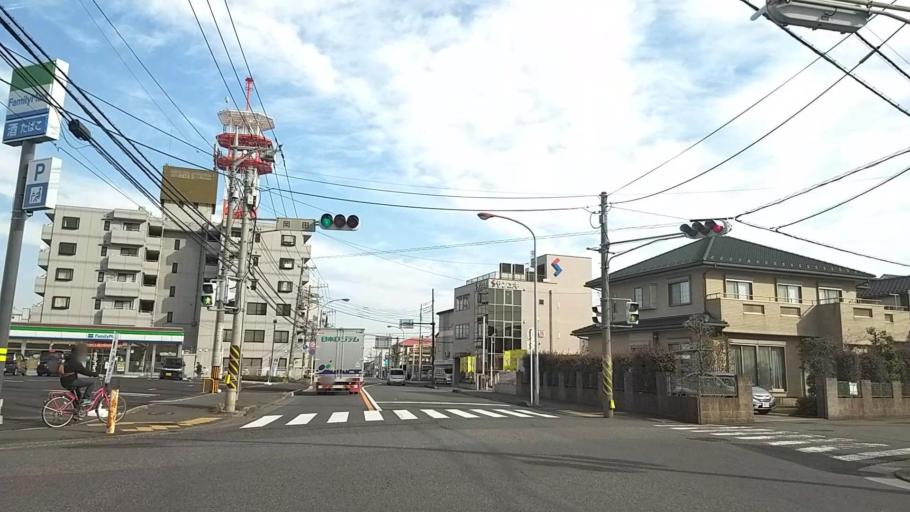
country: JP
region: Kanagawa
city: Atsugi
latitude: 35.4163
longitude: 139.3638
